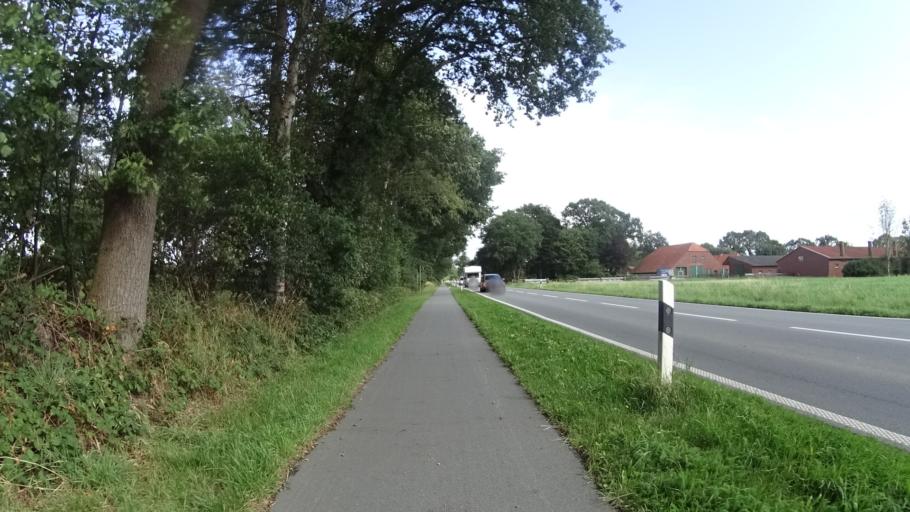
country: DE
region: Lower Saxony
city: Bockhorn
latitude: 53.3890
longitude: 8.0407
